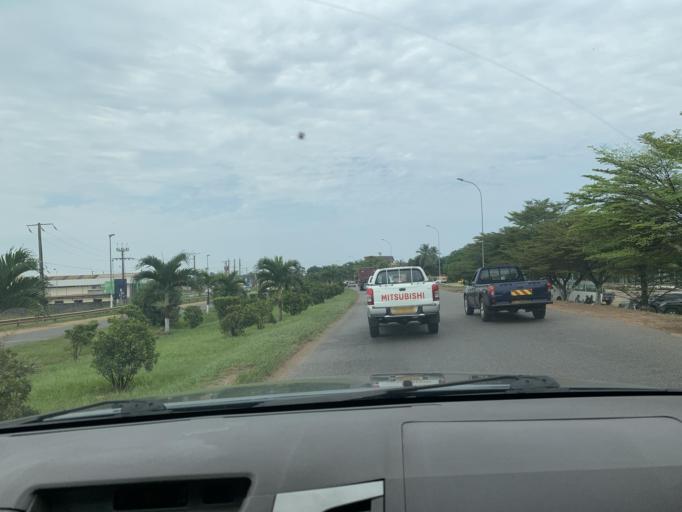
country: GA
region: Estuaire
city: Libreville
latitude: 0.3410
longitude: 9.4766
